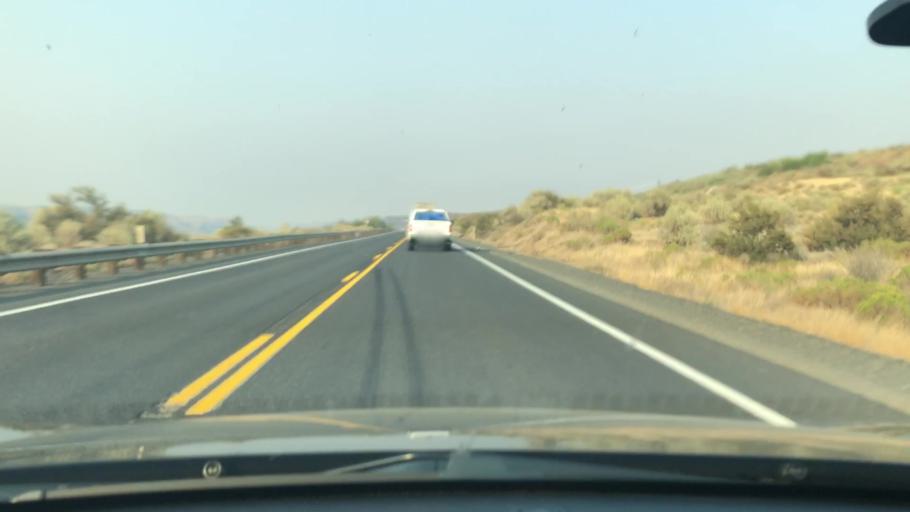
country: US
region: Oregon
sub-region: Umatilla County
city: Stanfield
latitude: 45.9251
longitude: -119.1087
